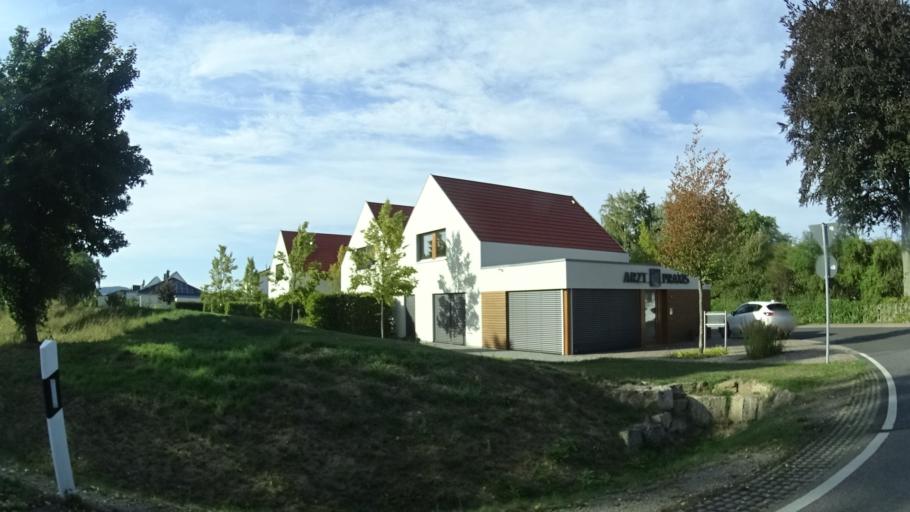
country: DE
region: Hesse
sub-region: Regierungsbezirk Kassel
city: Dipperz
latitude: 50.5431
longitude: 9.7895
